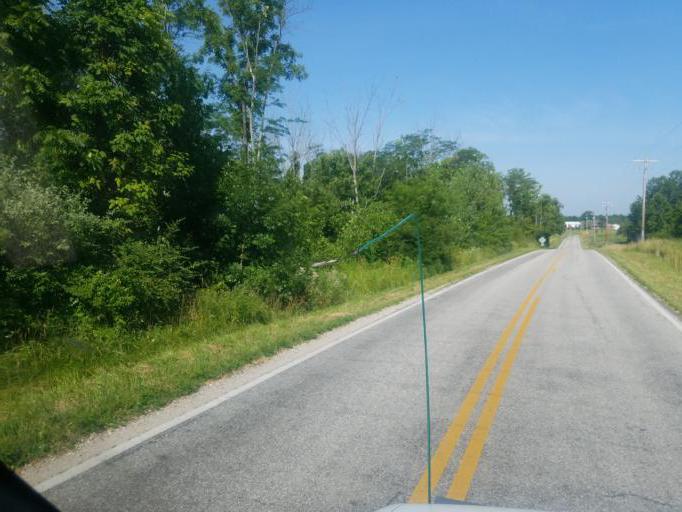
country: US
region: Ohio
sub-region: Union County
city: New California
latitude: 40.2818
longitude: -83.2278
